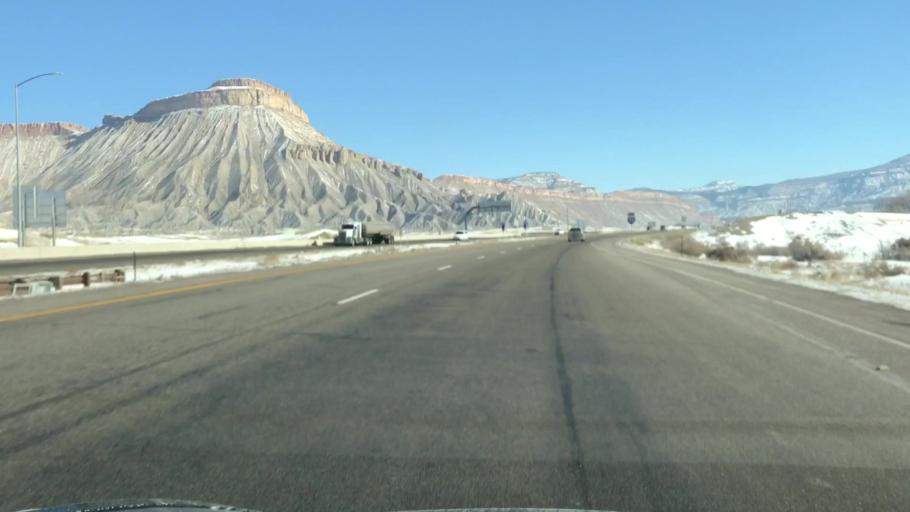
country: US
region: Colorado
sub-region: Mesa County
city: Clifton
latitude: 39.1070
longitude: -108.4405
